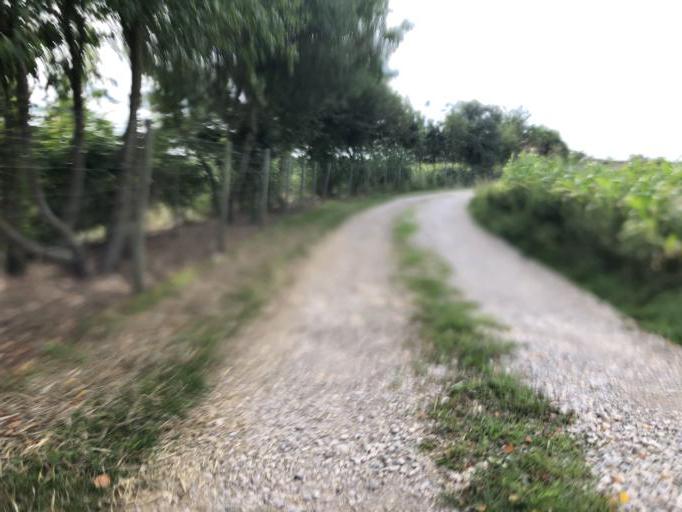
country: DE
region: Bavaria
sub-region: Regierungsbezirk Mittelfranken
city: Furth
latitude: 49.5267
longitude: 11.0015
